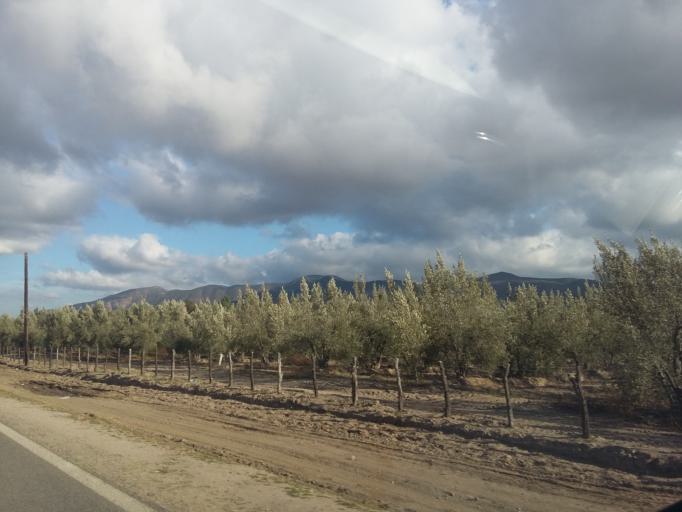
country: MX
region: Baja California
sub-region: Ensenada
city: Rancho Verde
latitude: 32.0793
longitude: -116.6149
